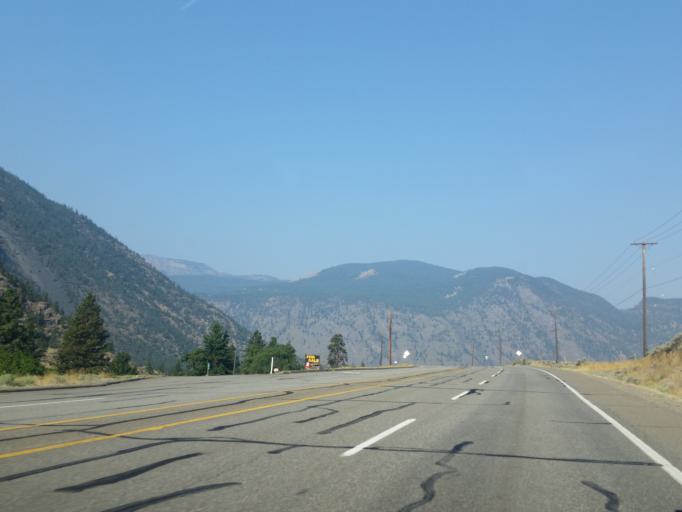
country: CA
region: British Columbia
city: Oliver
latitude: 49.2207
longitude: -119.9398
